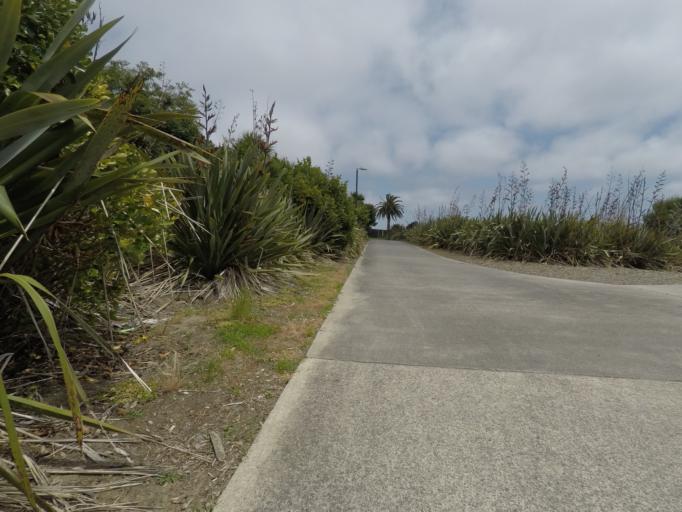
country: NZ
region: Auckland
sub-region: Auckland
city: Auckland
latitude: -36.9063
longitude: 174.7274
